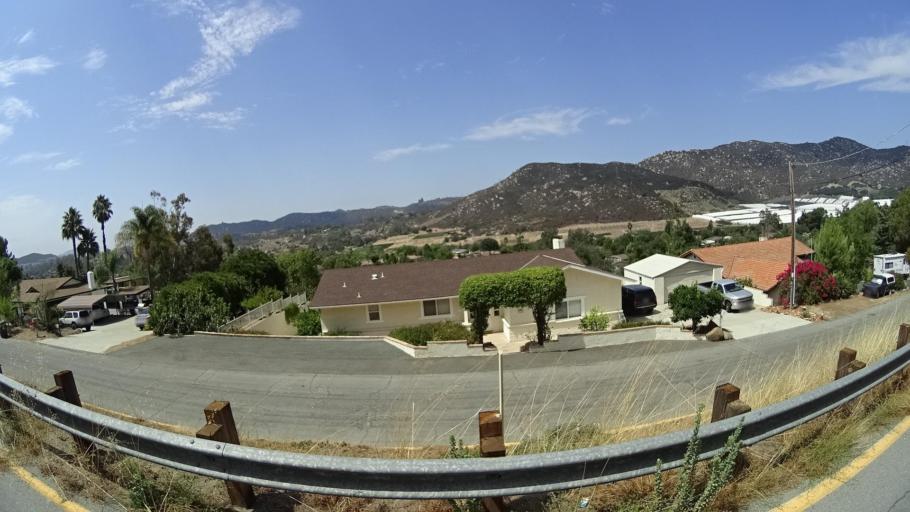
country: US
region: California
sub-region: San Diego County
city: Hidden Meadows
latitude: 33.1857
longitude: -117.0878
